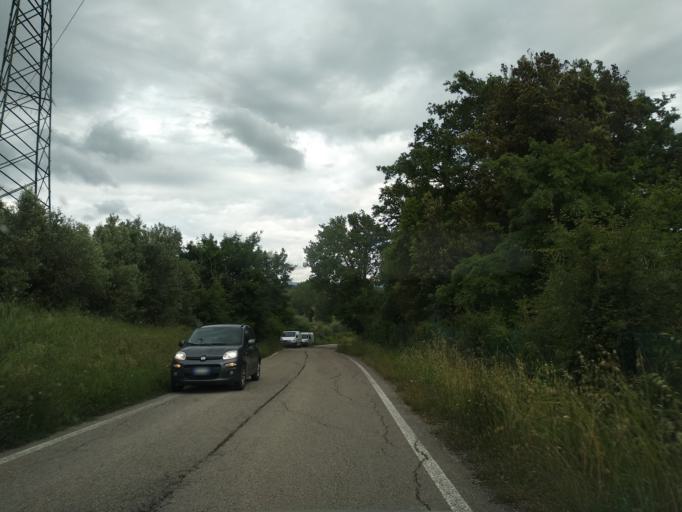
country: IT
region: Tuscany
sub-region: Provincia di Livorno
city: Collesalvetti
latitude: 43.5396
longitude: 10.4569
